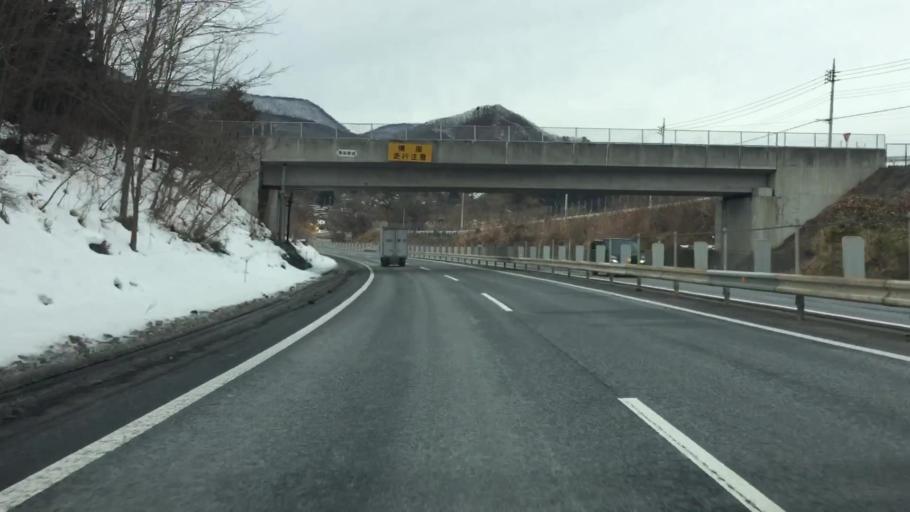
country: JP
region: Gunma
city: Numata
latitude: 36.7082
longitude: 138.9825
